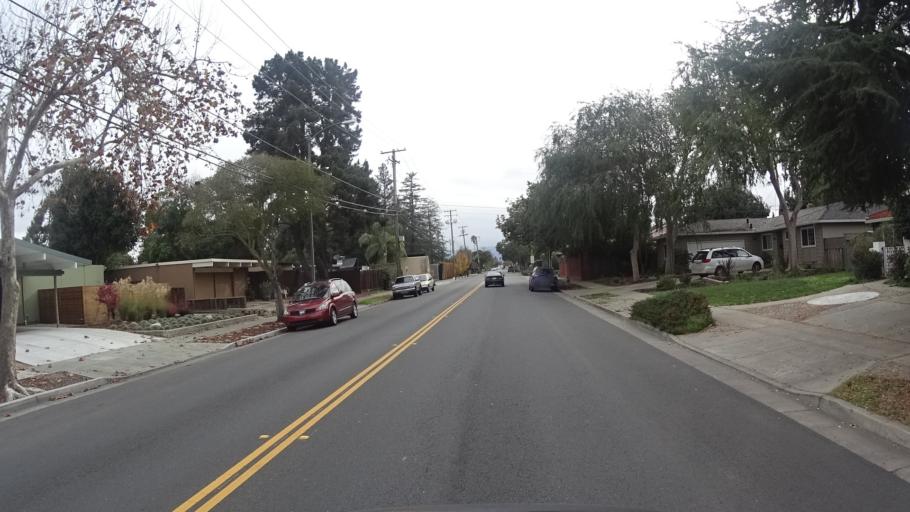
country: US
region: California
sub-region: Santa Clara County
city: Sunnyvale
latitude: 37.3581
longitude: -122.0415
